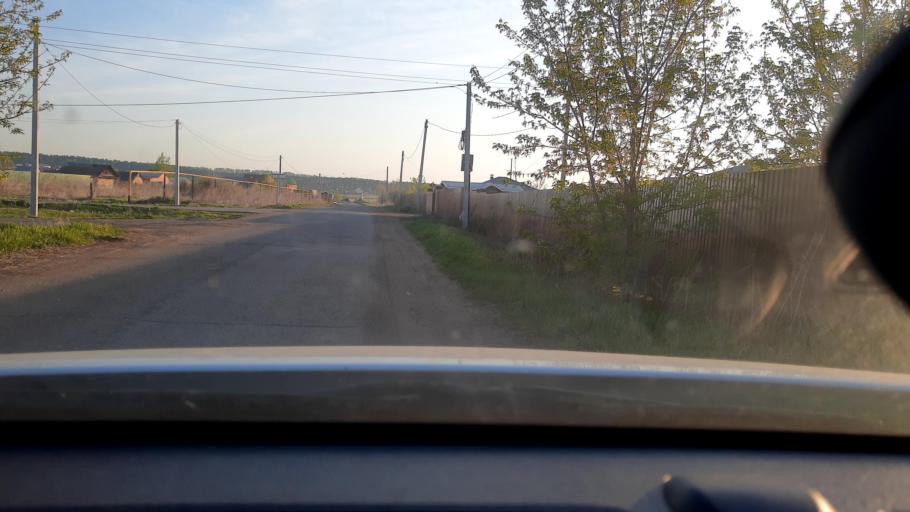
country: RU
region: Bashkortostan
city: Avdon
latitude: 54.5061
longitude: 55.8154
